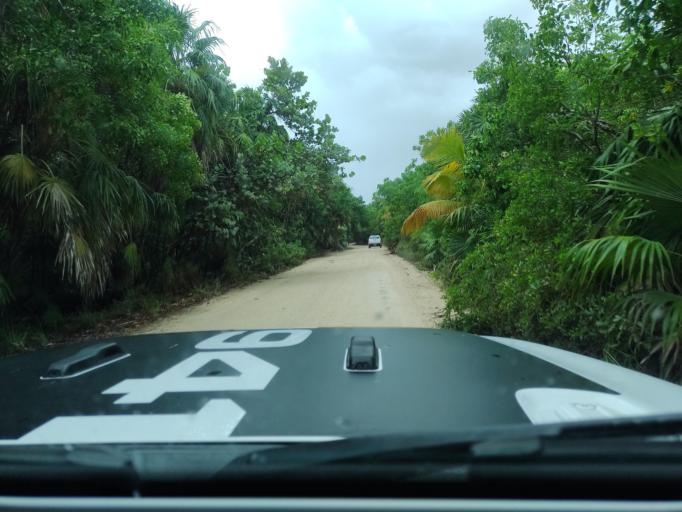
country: MX
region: Quintana Roo
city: Tulum
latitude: 20.0585
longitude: -87.4809
